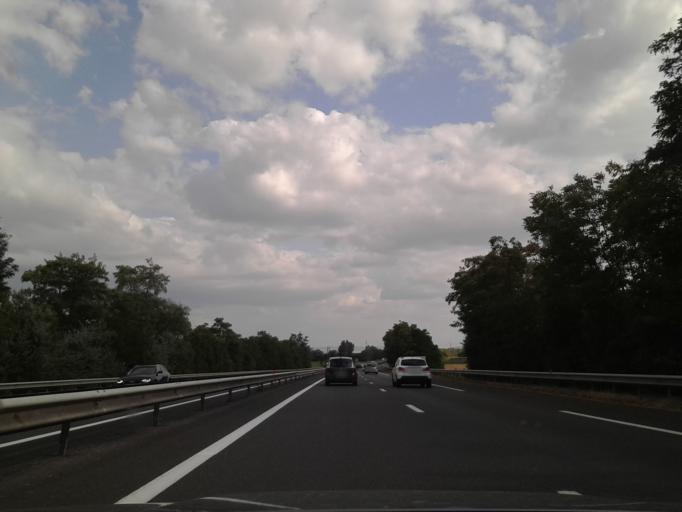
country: FR
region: Auvergne
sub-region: Departement du Puy-de-Dome
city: Riom
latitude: 45.9147
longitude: 3.1514
